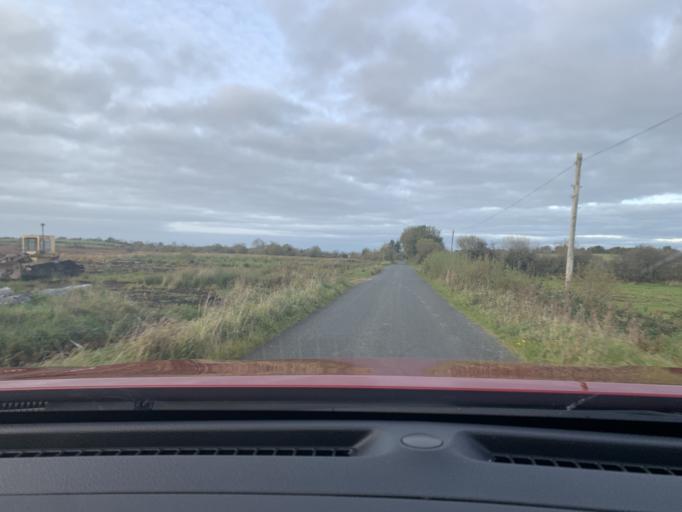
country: IE
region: Connaught
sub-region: Roscommon
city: Ballaghaderreen
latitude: 53.9950
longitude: -8.6086
